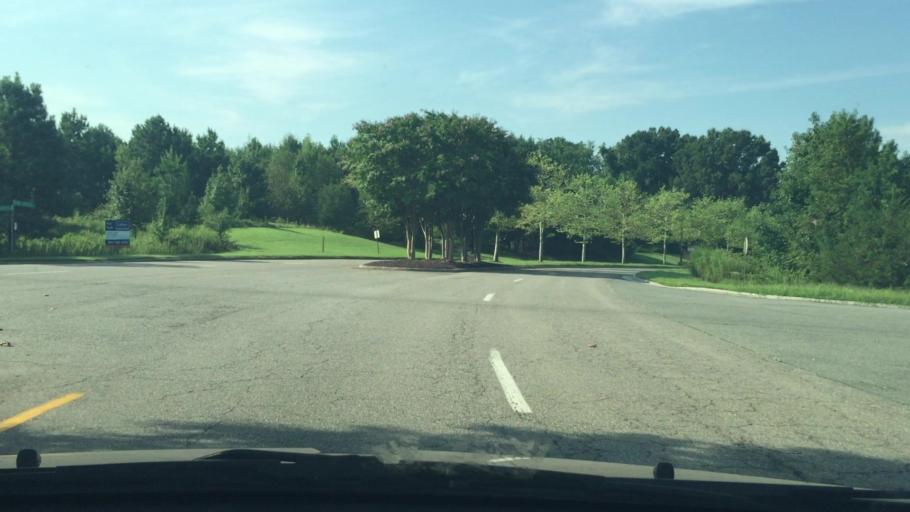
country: US
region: Virginia
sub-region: Henrico County
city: Chamberlayne
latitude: 37.6461
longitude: -77.4036
